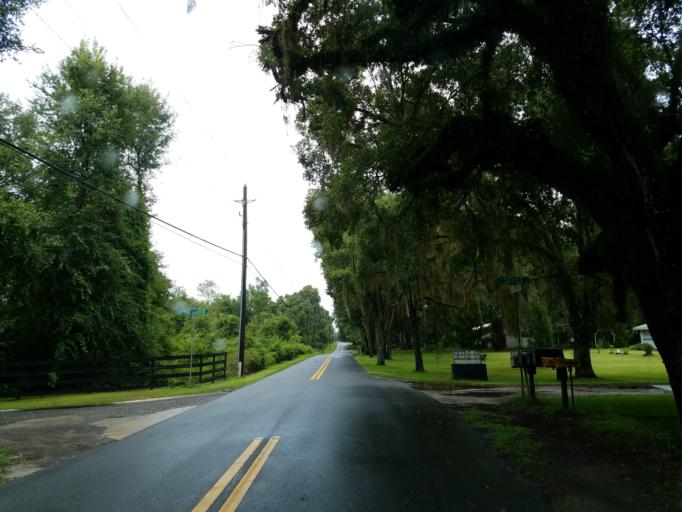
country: US
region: Florida
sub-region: Citrus County
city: Floral City
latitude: 28.7924
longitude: -82.2951
